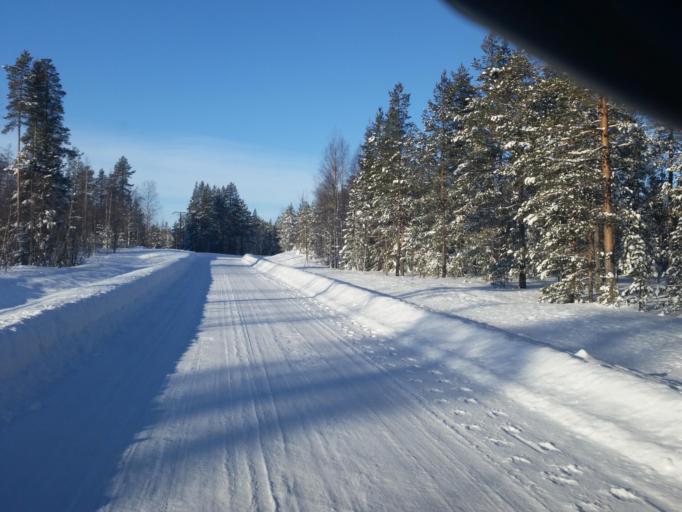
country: SE
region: Vaesterbotten
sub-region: Skelleftea Kommun
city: Backa
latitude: 65.1991
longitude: 21.0076
